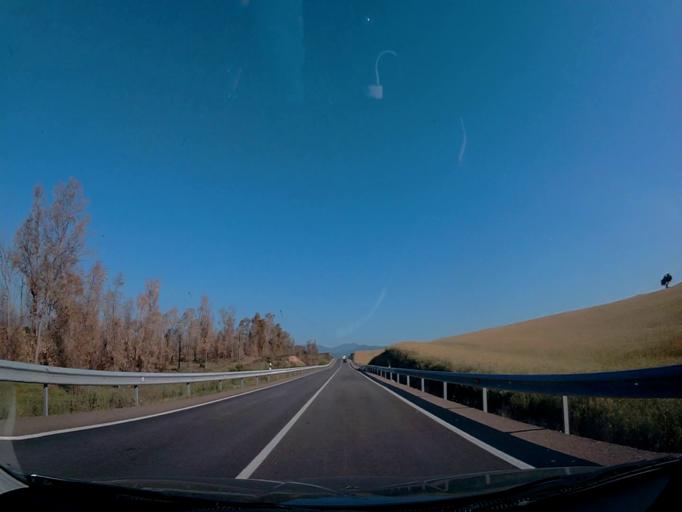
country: ES
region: Castille-La Mancha
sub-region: Province of Toledo
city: Hormigos
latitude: 40.1152
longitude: -4.4043
